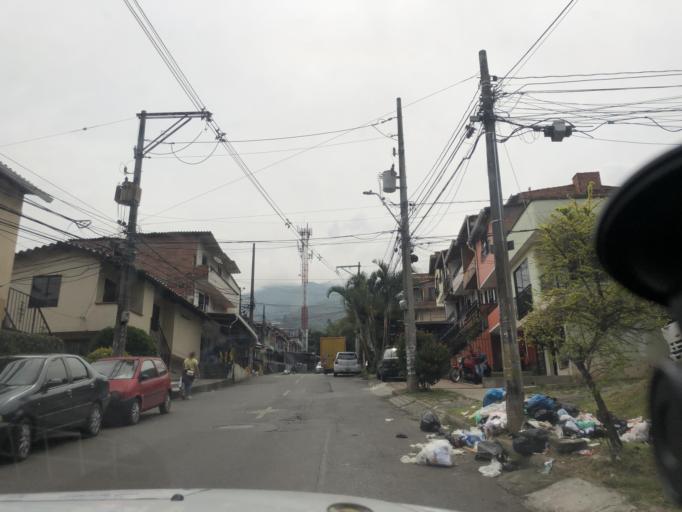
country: CO
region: Antioquia
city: Bello
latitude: 6.3319
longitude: -75.5386
